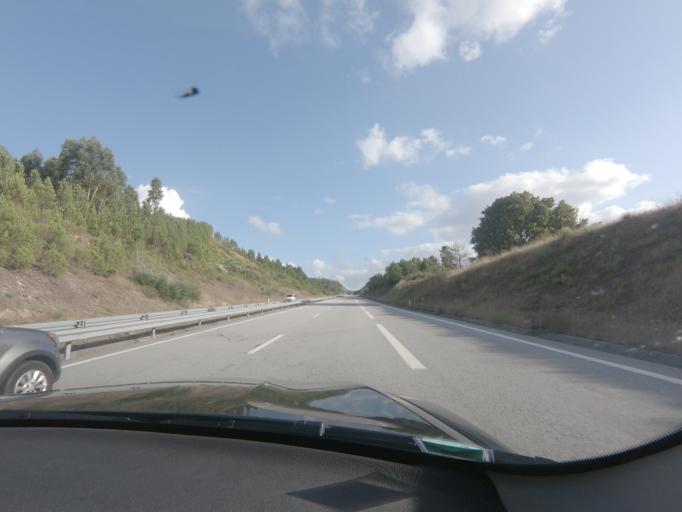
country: PT
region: Viseu
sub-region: Viseu
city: Campo
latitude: 40.7906
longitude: -7.9287
